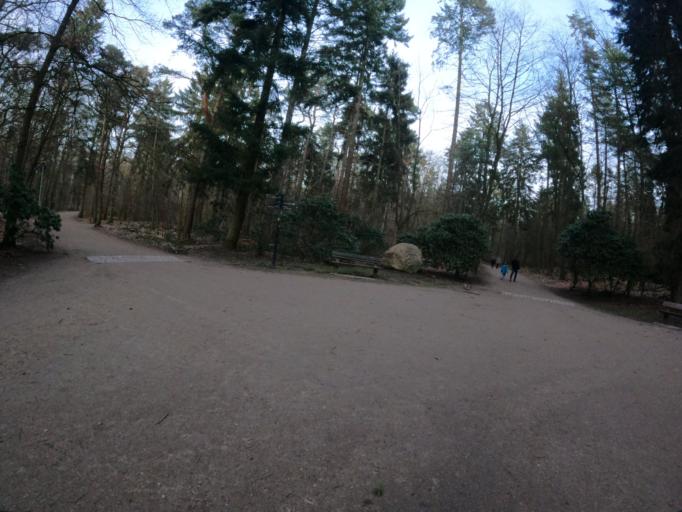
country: DE
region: Hamburg
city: Eidelstedt
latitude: 53.5817
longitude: 9.8918
